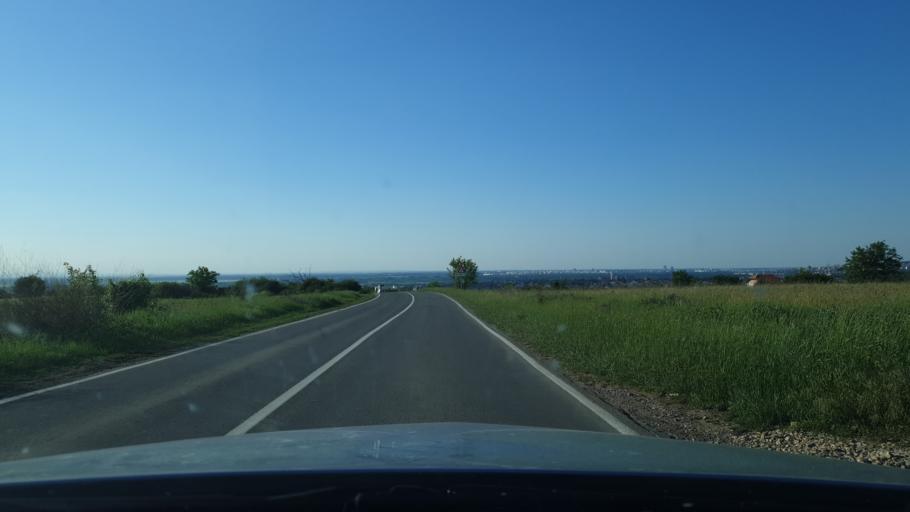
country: RS
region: Central Serbia
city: Sremcica
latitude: 44.6986
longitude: 20.3779
